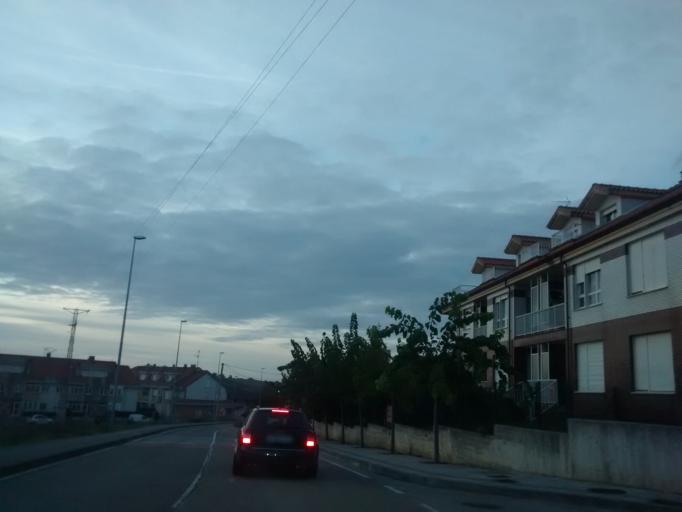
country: ES
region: Cantabria
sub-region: Provincia de Cantabria
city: Santa Cruz de Bezana
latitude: 43.4282
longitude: -3.9417
